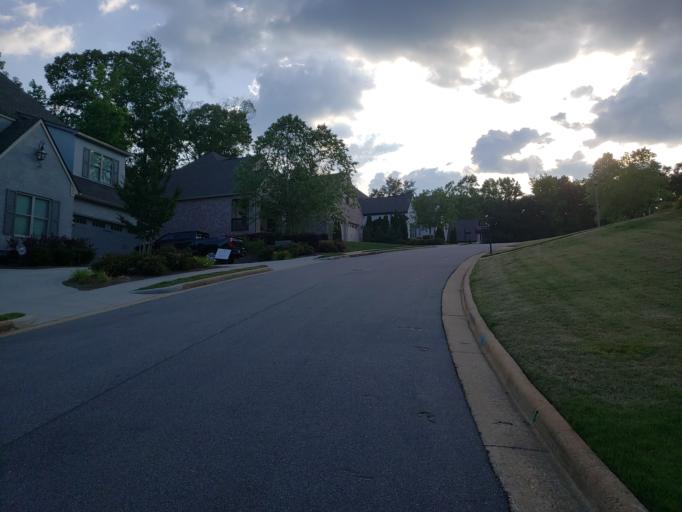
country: US
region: Alabama
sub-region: Lee County
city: Auburn
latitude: 32.5852
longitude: -85.4535
